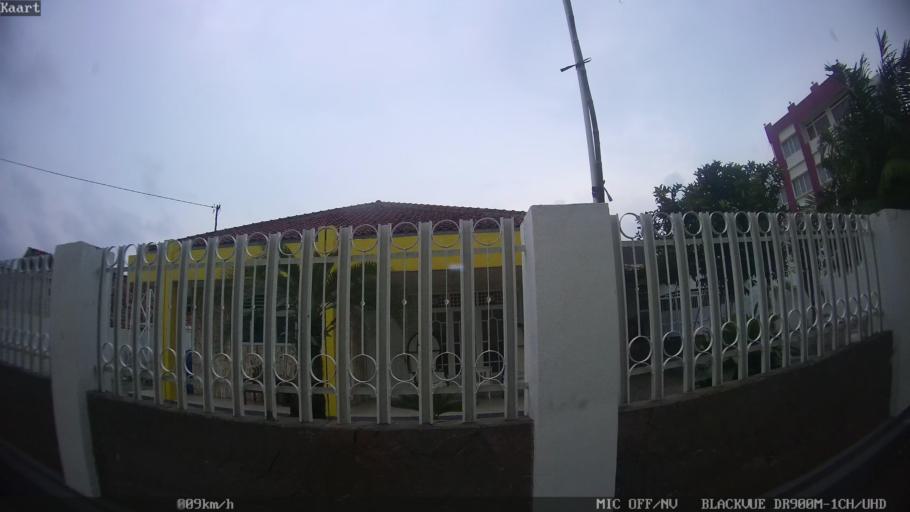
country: ID
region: Lampung
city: Kedaton
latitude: -5.4032
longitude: 105.2677
